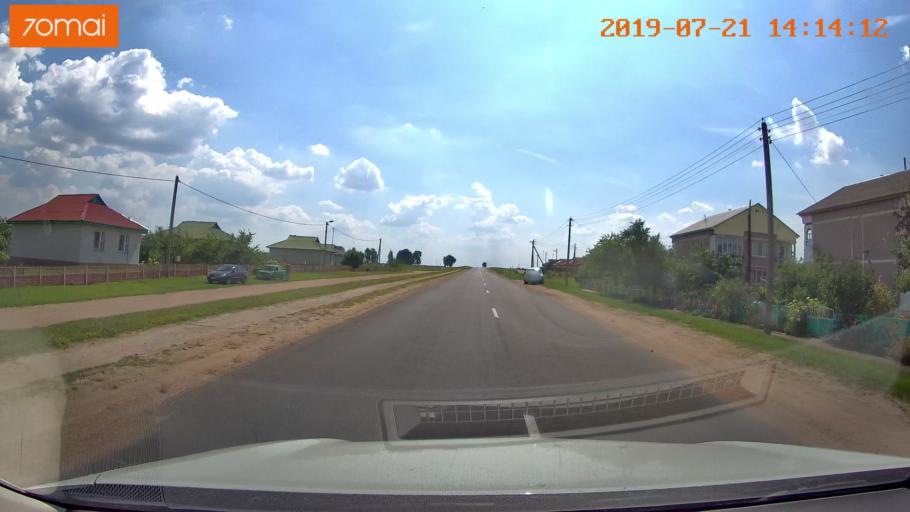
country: BY
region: Grodnenskaya
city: Karelichy
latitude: 53.6492
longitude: 26.1690
